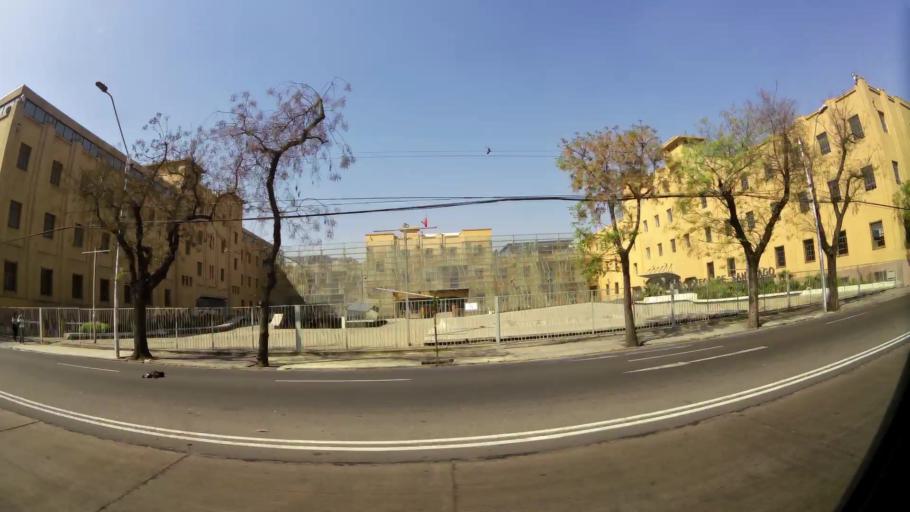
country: CL
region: Santiago Metropolitan
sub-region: Provincia de Santiago
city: Santiago
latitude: -33.4446
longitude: -70.6795
